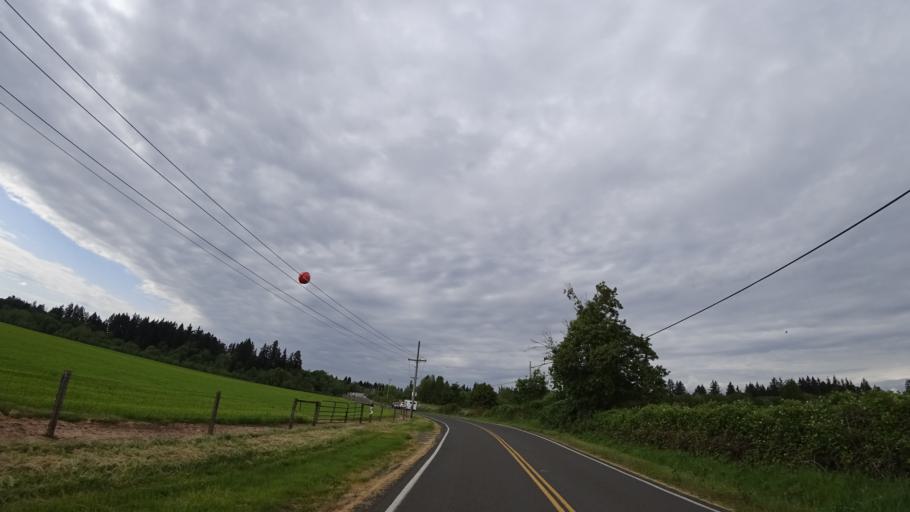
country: US
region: Oregon
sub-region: Washington County
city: Hillsboro
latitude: 45.4863
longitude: -122.9498
